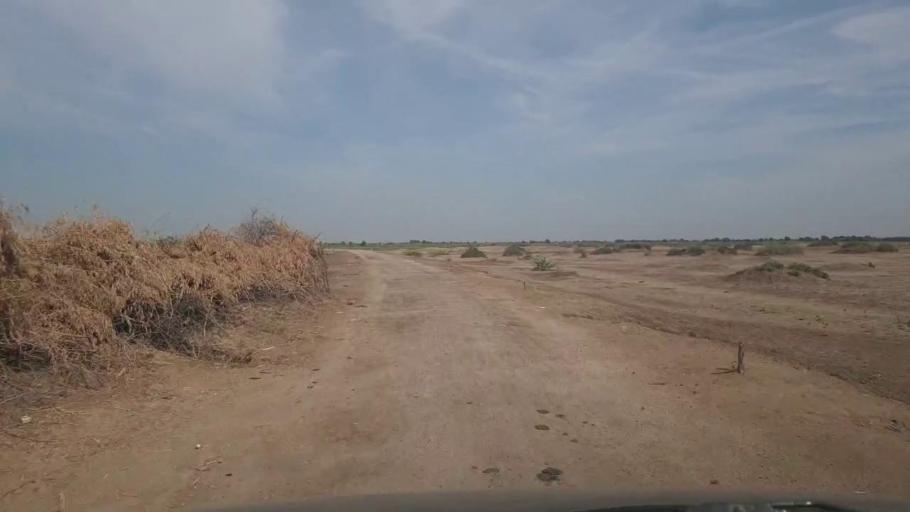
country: PK
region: Sindh
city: Kunri
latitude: 25.2326
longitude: 69.6236
